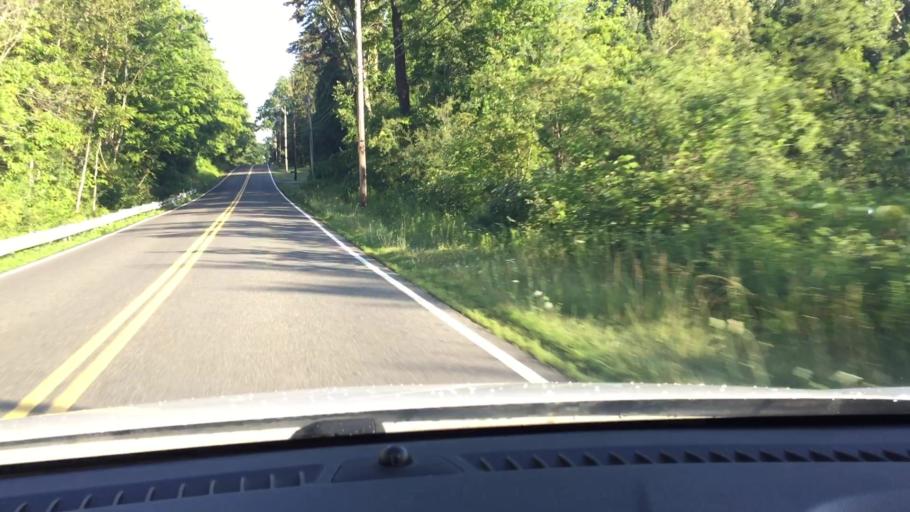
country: US
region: Massachusetts
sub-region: Berkshire County
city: Lenox
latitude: 42.3416
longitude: -73.2589
